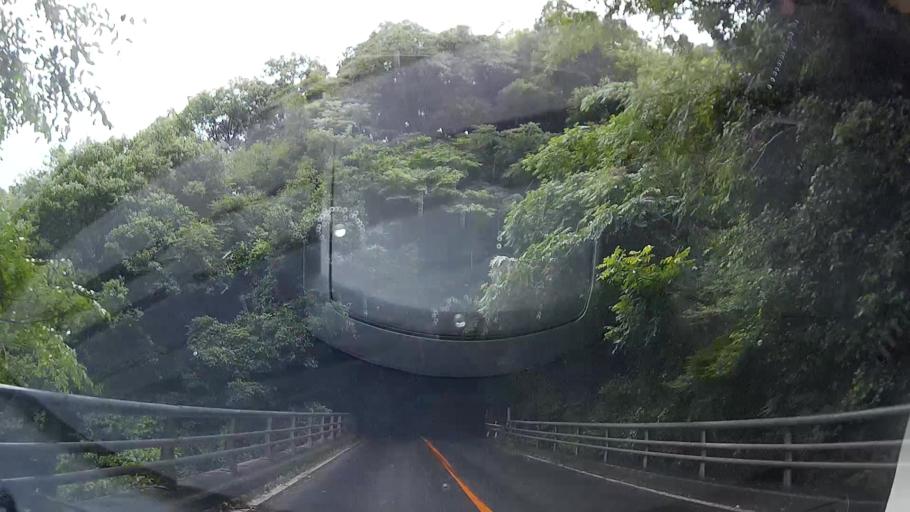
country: JP
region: Oita
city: Hita
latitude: 33.1819
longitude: 131.0024
